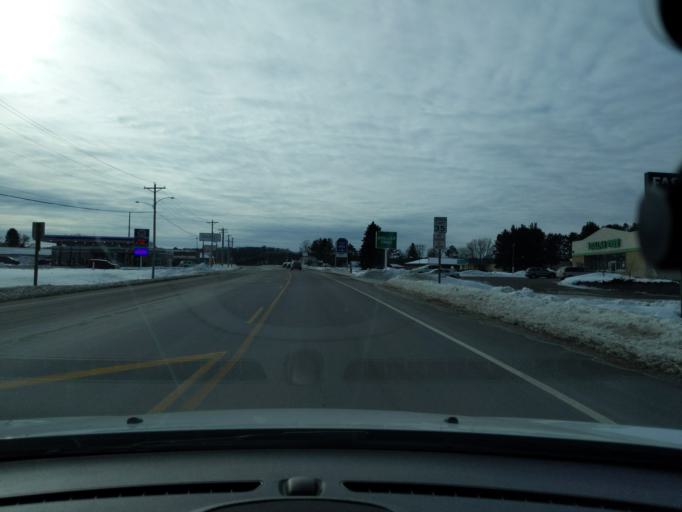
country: US
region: Wisconsin
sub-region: Washburn County
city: Spooner
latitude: 45.8167
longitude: -91.8959
